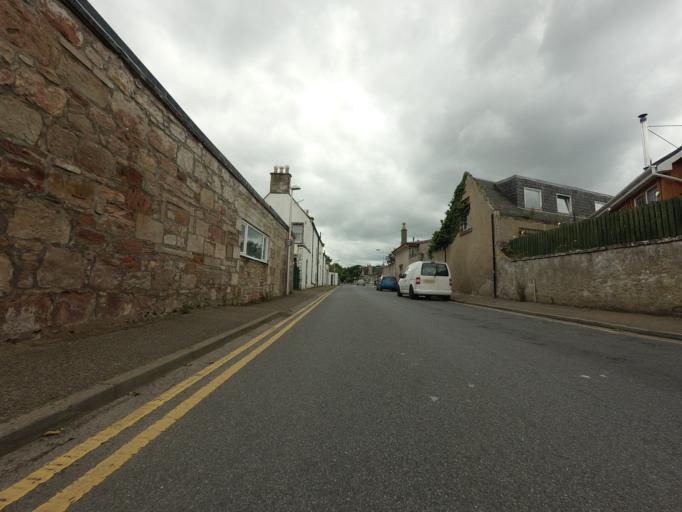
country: GB
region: Scotland
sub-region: Highland
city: Nairn
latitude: 57.5829
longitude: -3.8716
